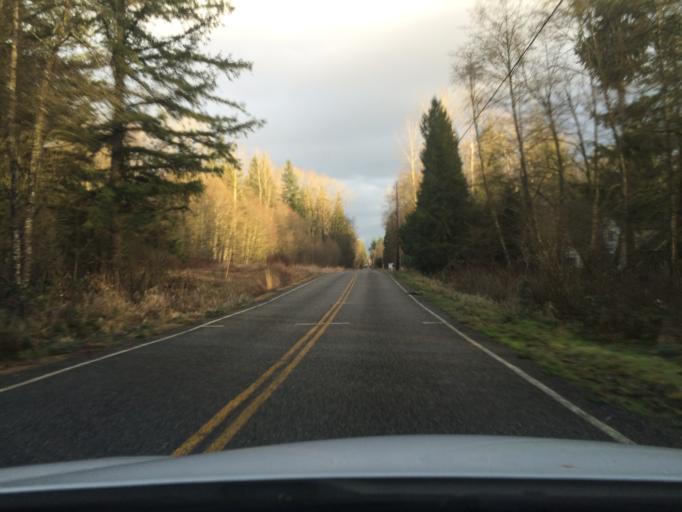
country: CA
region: British Columbia
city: Langley
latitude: 48.9936
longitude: -122.6045
